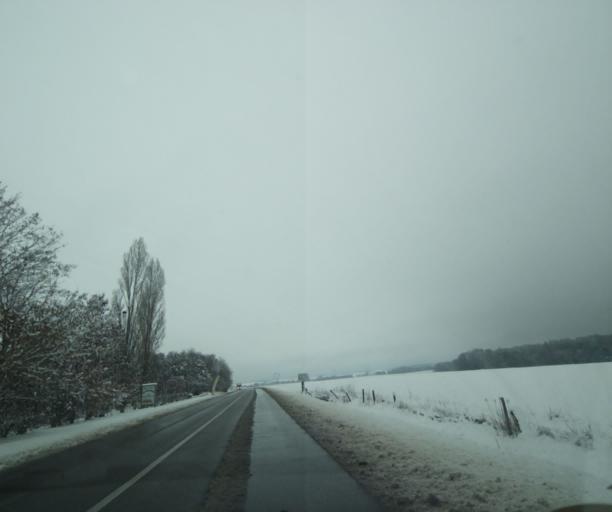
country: FR
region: Champagne-Ardenne
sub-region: Departement de la Haute-Marne
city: Montier-en-Der
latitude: 48.4926
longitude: 4.7796
